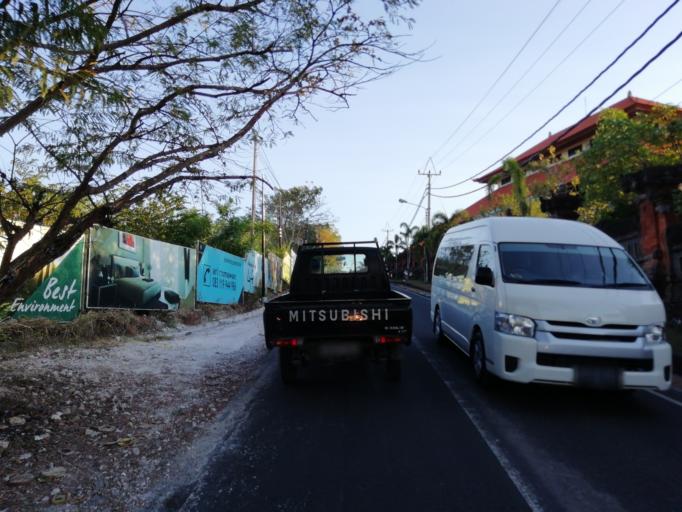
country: ID
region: Bali
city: Bualu
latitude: -8.8104
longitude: 115.1935
